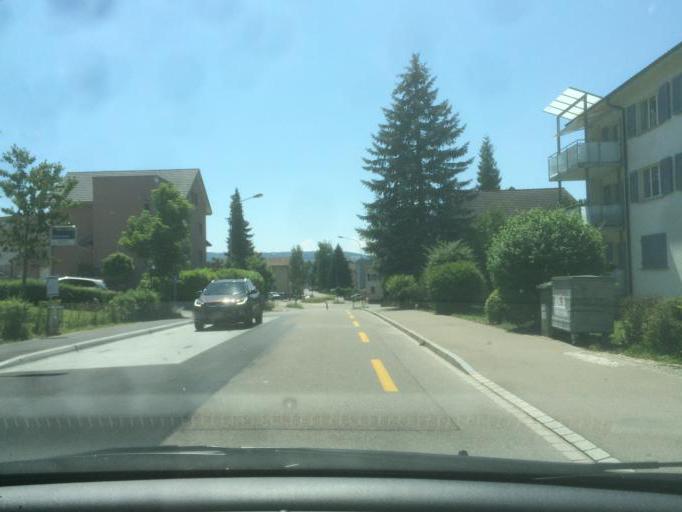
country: CH
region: Zurich
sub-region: Bezirk Uster
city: Uster / Gschwader
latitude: 47.3584
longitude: 8.7129
